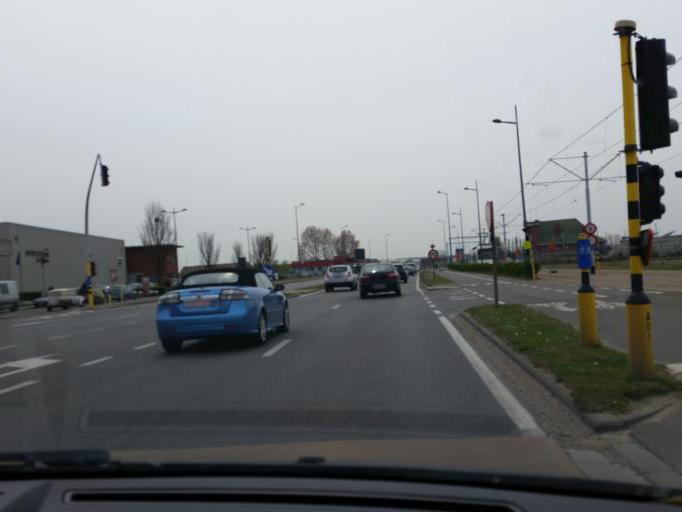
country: BE
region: Flanders
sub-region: Provincie West-Vlaanderen
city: Ostend
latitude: 51.2270
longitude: 2.9412
